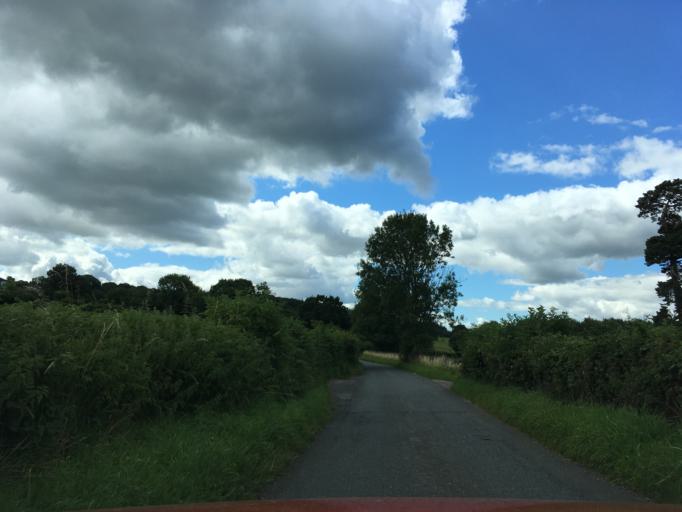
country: GB
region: England
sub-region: Gloucestershire
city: Cinderford
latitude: 51.8170
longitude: -2.4816
